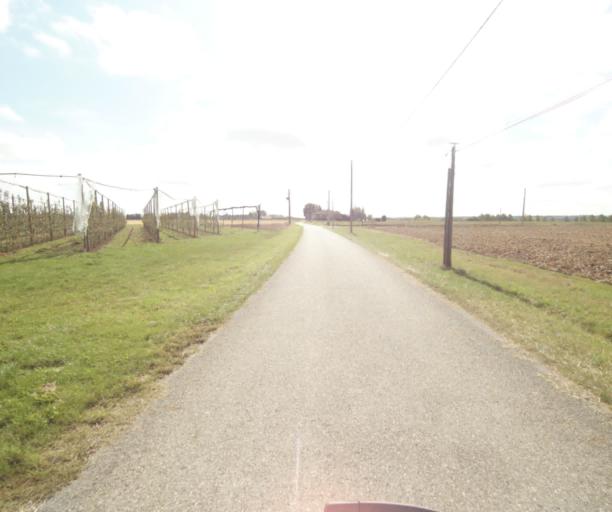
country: FR
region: Midi-Pyrenees
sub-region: Departement du Tarn-et-Garonne
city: Finhan
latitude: 43.9378
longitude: 1.2167
